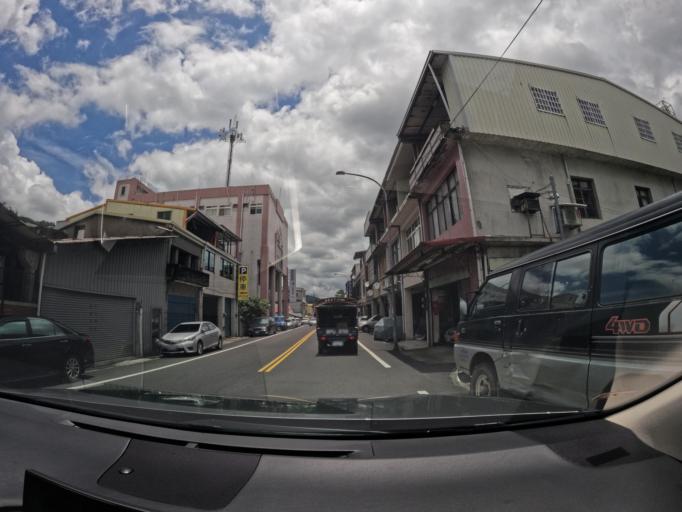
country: TW
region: Taiwan
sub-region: Miaoli
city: Miaoli
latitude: 24.6021
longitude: 120.9998
